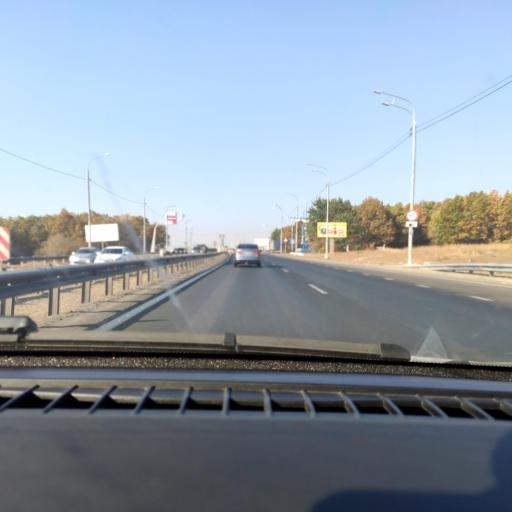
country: RU
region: Voronezj
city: Pridonskoy
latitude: 51.6523
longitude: 39.0497
